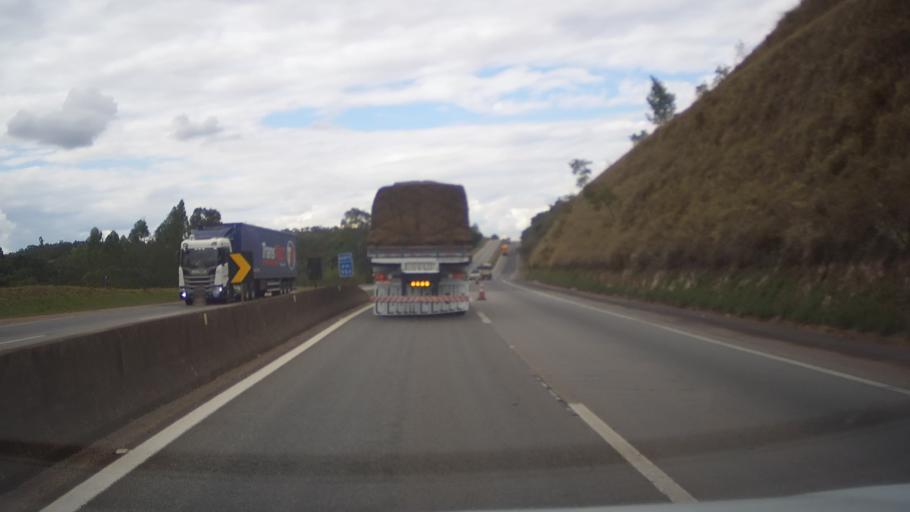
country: BR
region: Minas Gerais
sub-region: Itauna
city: Itauna
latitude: -20.3215
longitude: -44.4562
